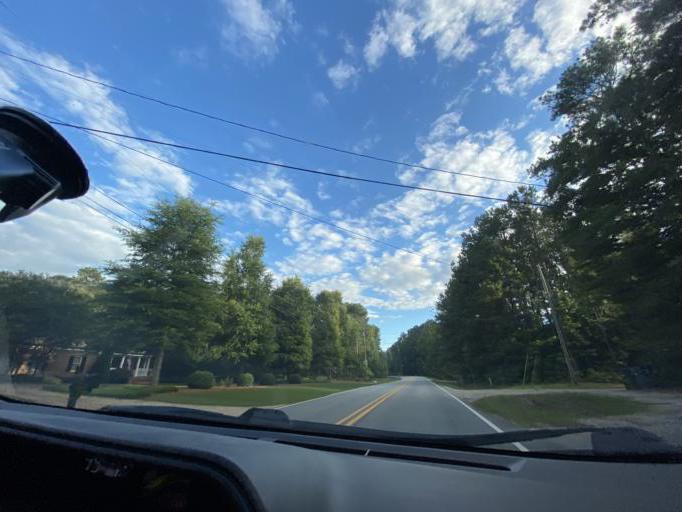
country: US
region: Georgia
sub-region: Fayette County
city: Peachtree City
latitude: 33.4286
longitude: -84.6491
